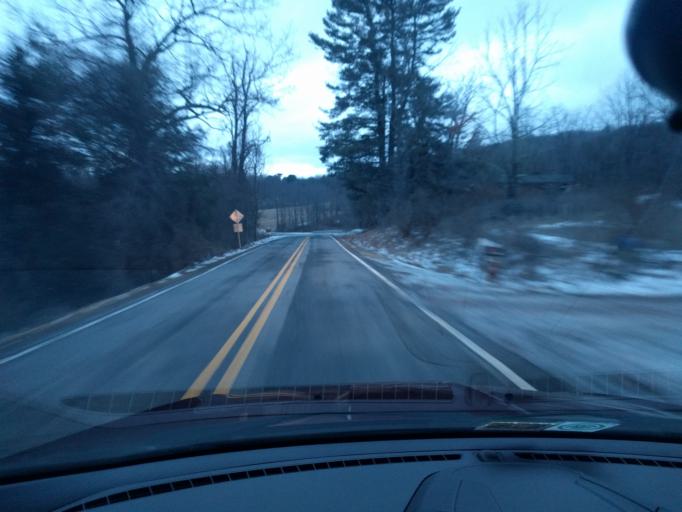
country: US
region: Virginia
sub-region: Alleghany County
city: Clifton Forge
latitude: 37.8998
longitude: -79.8902
